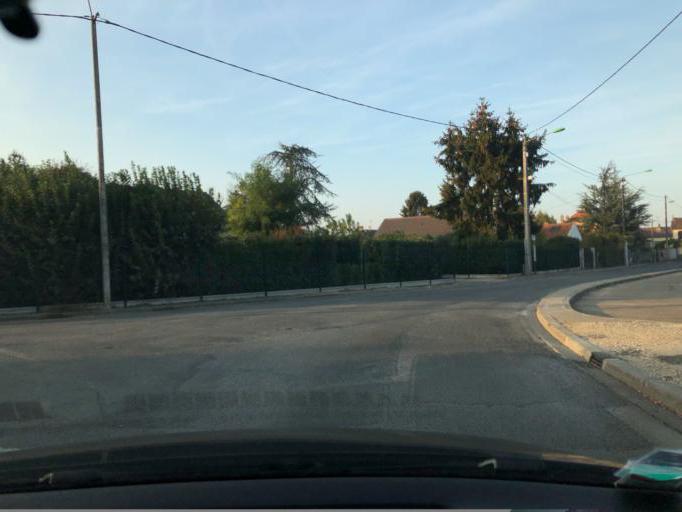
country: FR
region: Bourgogne
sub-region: Departement de l'Yonne
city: Saint-Clement
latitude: 48.2138
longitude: 3.2914
